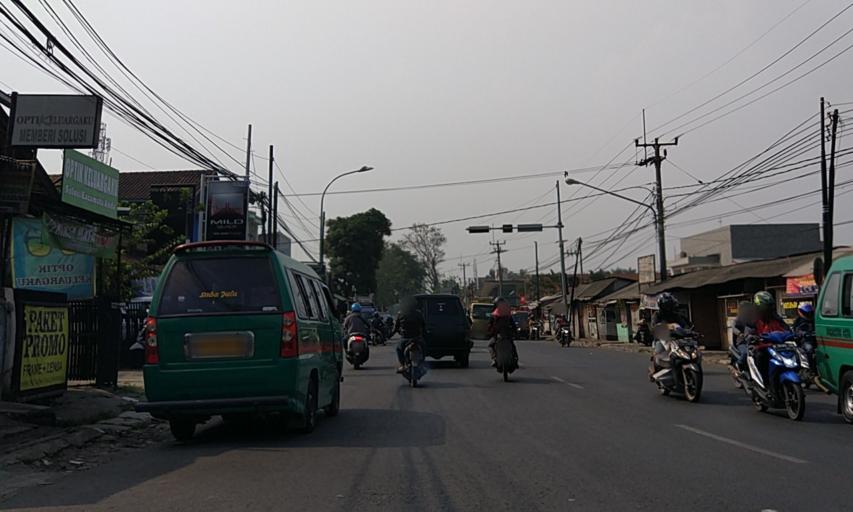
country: ID
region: West Java
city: Margahayukencana
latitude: -6.9989
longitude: 107.5537
